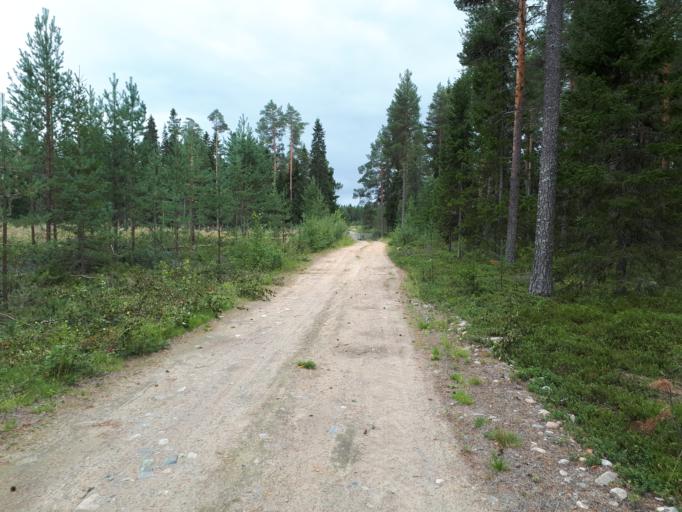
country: FI
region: Northern Ostrobothnia
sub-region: Oulunkaari
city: Ii
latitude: 65.3030
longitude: 25.4172
